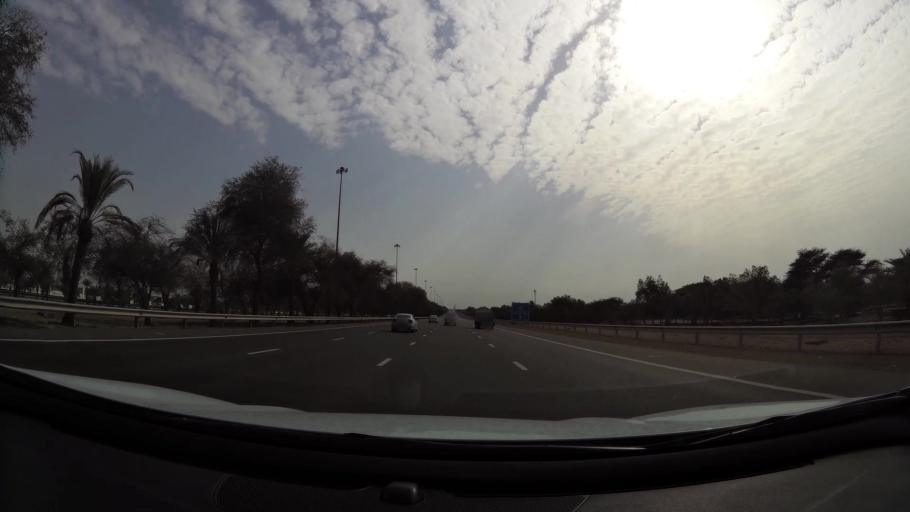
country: AE
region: Abu Dhabi
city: Abu Dhabi
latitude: 24.4982
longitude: 54.6804
